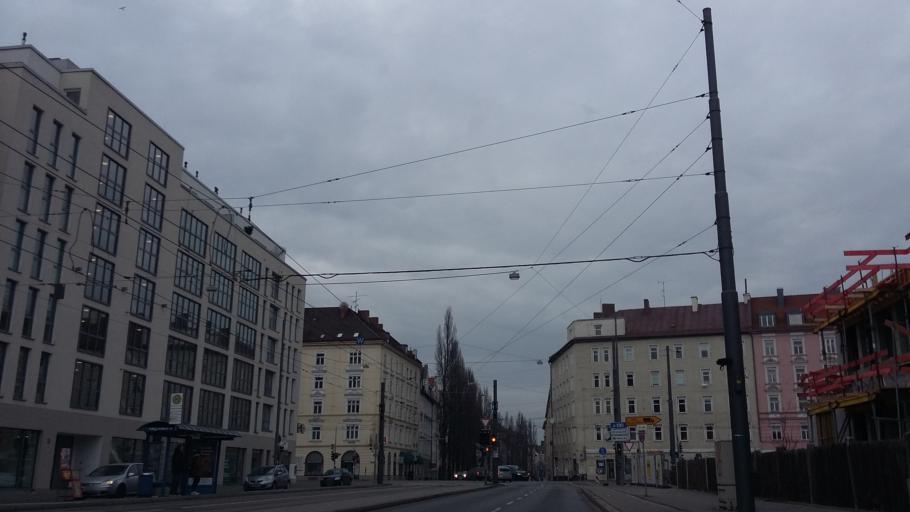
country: DE
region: Bavaria
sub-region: Upper Bavaria
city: Bogenhausen
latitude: 48.1356
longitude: 11.6097
